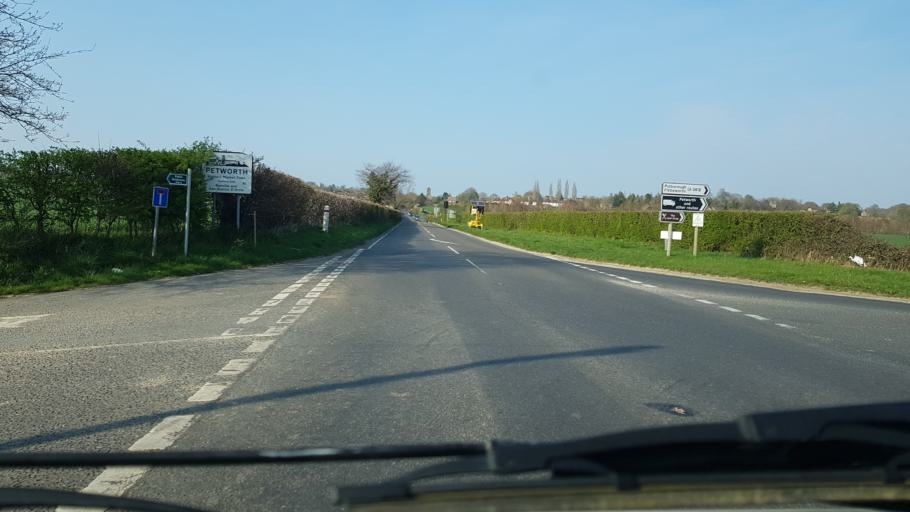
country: GB
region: England
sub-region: West Sussex
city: Petworth
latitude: 50.9754
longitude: -0.6134
